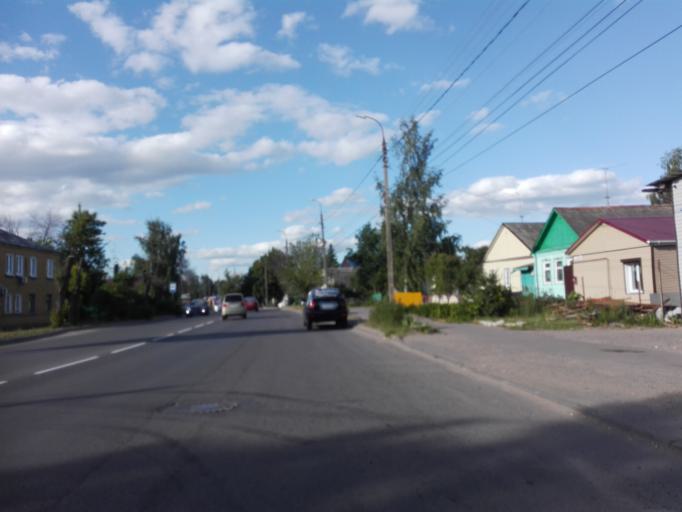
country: RU
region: Orjol
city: Orel
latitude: 52.9436
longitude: 36.0741
